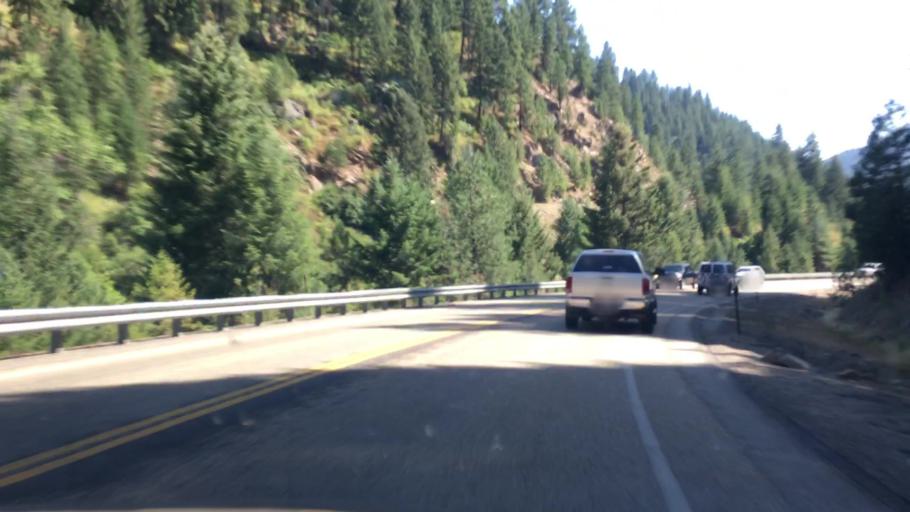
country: US
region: Idaho
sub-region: Valley County
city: Cascade
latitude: 44.1494
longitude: -116.1120
